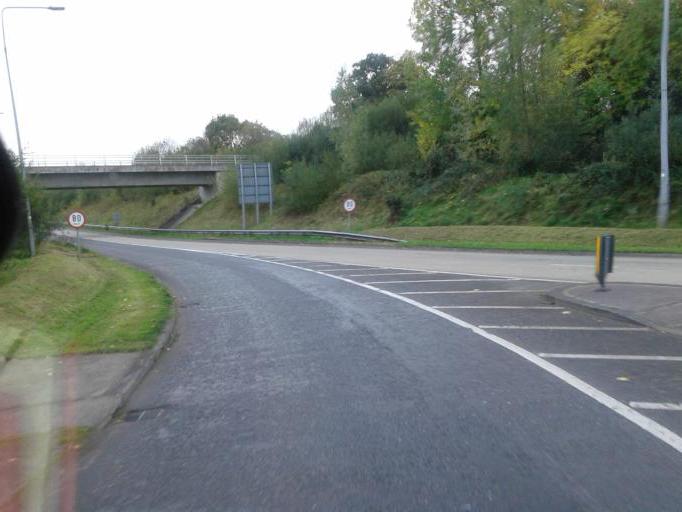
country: IE
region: Munster
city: Ballina
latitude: 52.7688
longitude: -8.4292
